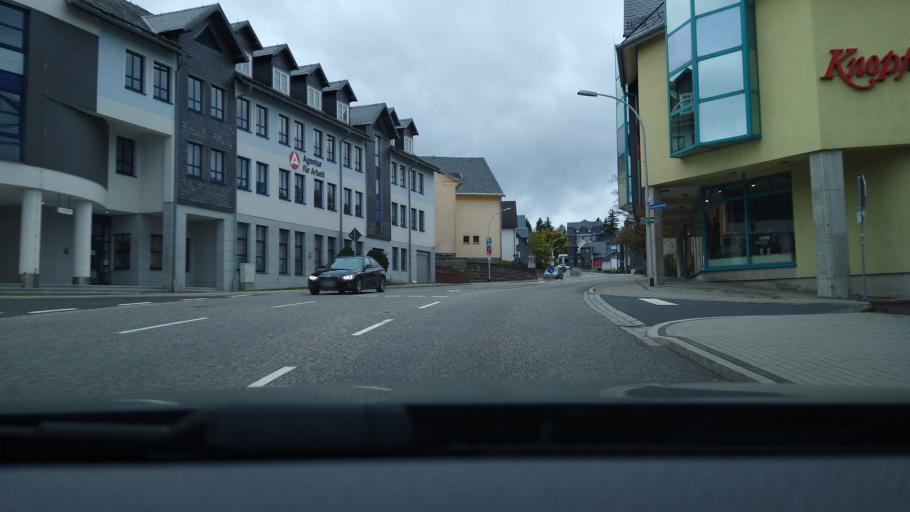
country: DE
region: Thuringia
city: Neuhaus am Rennweg
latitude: 50.5097
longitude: 11.1386
